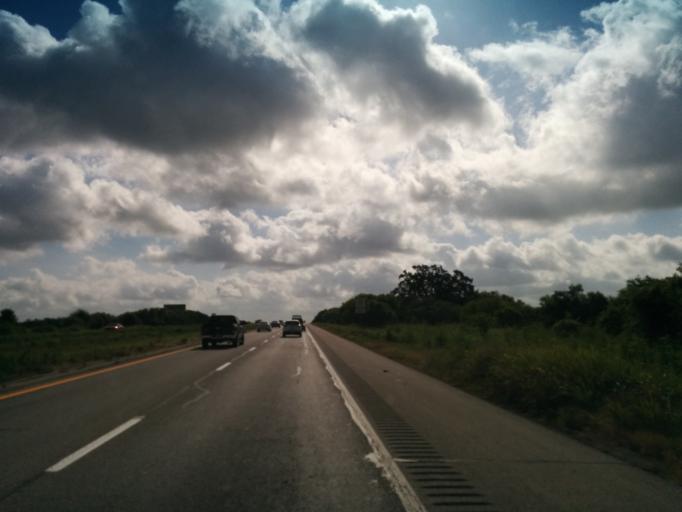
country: US
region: Texas
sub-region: Caldwell County
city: Luling
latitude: 29.6496
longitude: -97.6798
